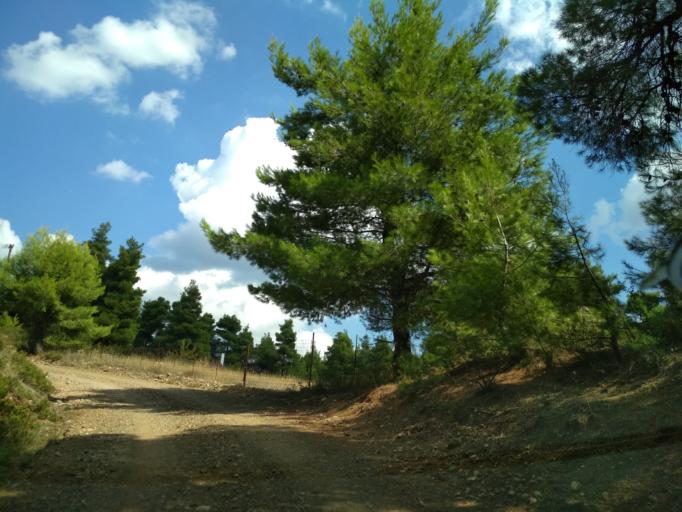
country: GR
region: Central Greece
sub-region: Nomos Evvoias
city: Roviai
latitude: 38.8368
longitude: 23.2787
